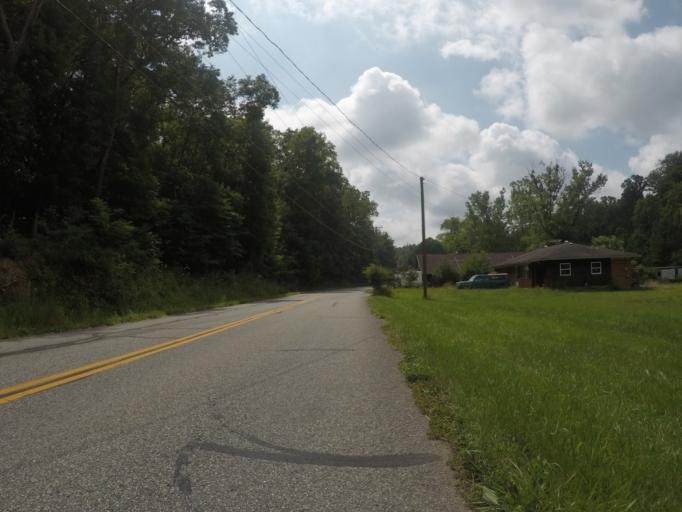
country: US
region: Kentucky
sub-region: Boyd County
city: Meads
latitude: 38.4168
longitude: -82.6906
